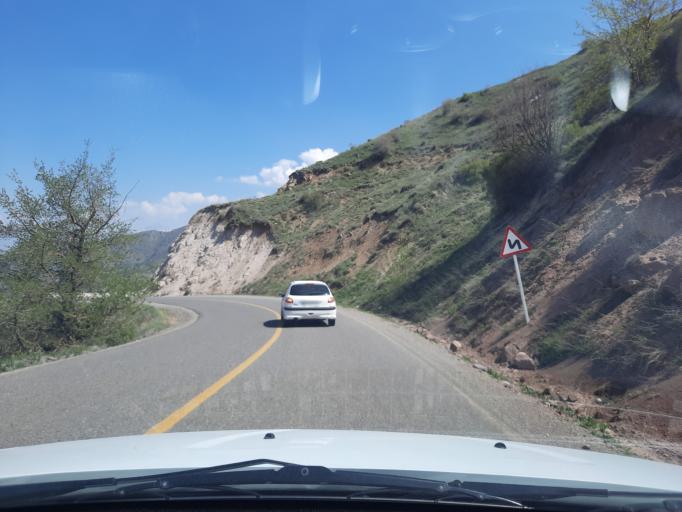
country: IR
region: Qazvin
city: Qazvin
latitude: 36.4138
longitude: 50.2400
